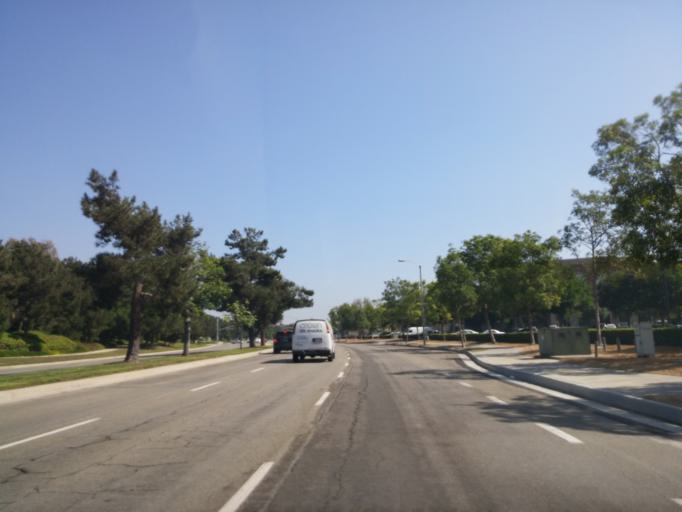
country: US
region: California
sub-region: Orange County
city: Irvine
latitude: 33.6871
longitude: -117.8162
